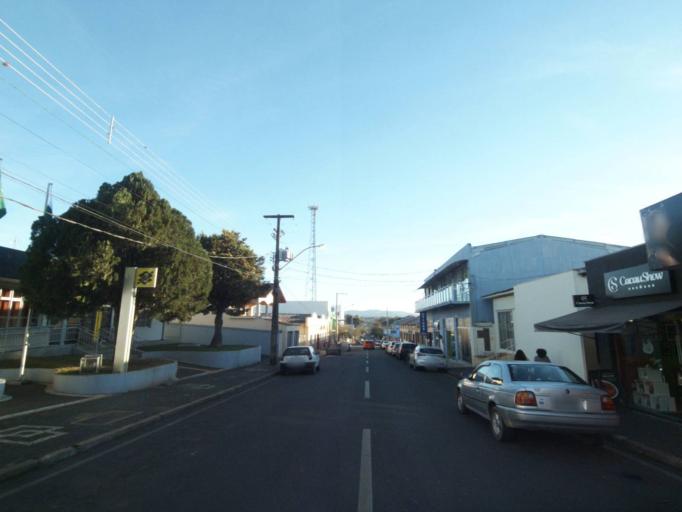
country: BR
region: Parana
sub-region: Tibagi
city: Tibagi
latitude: -24.5156
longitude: -50.4109
